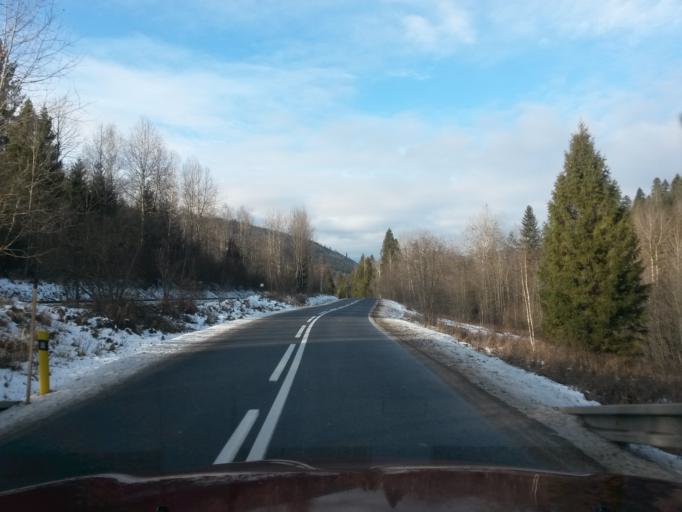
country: SK
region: Kosicky
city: Spisska Nova Ves
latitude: 48.8142
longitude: 20.6688
